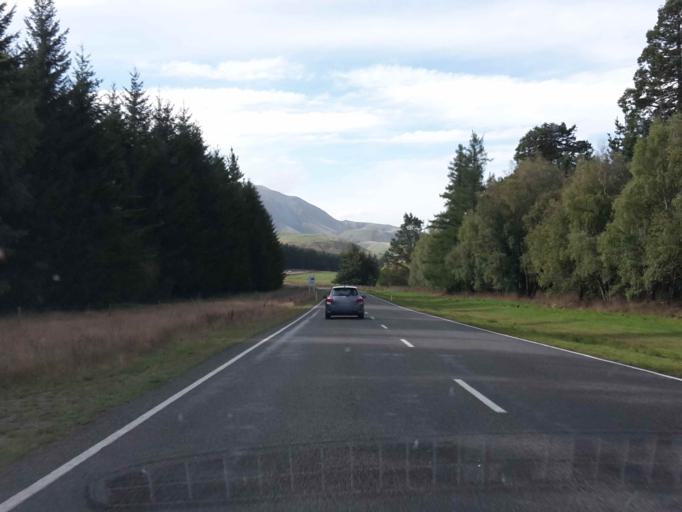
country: NZ
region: Canterbury
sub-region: Timaru District
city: Pleasant Point
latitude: -44.0447
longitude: 170.6840
